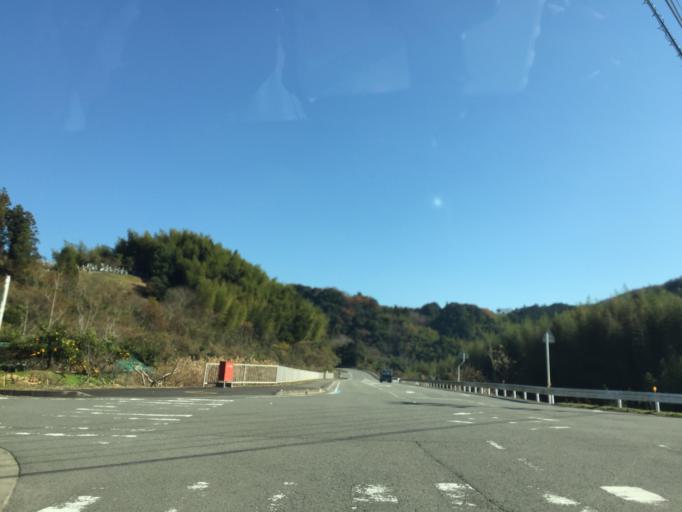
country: JP
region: Wakayama
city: Iwade
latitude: 34.1440
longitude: 135.3535
